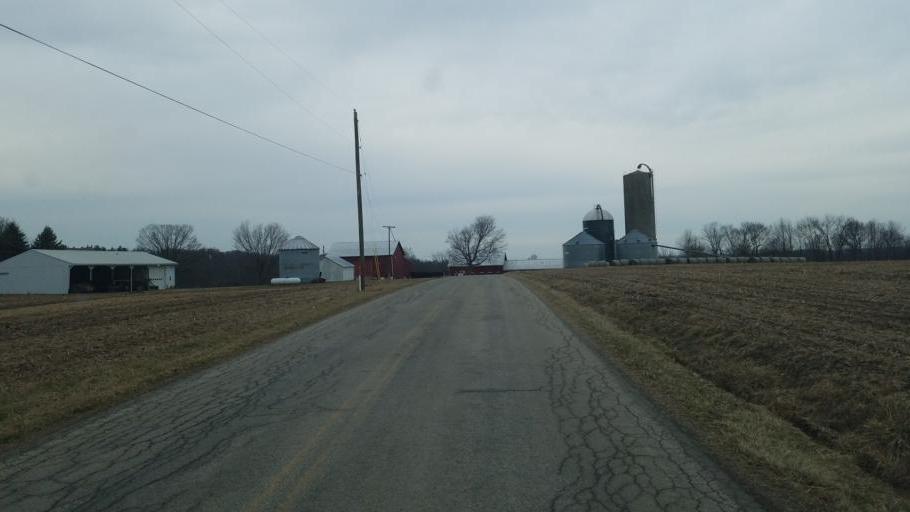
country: US
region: Ohio
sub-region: Richland County
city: Lincoln Heights
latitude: 40.7201
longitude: -82.3826
